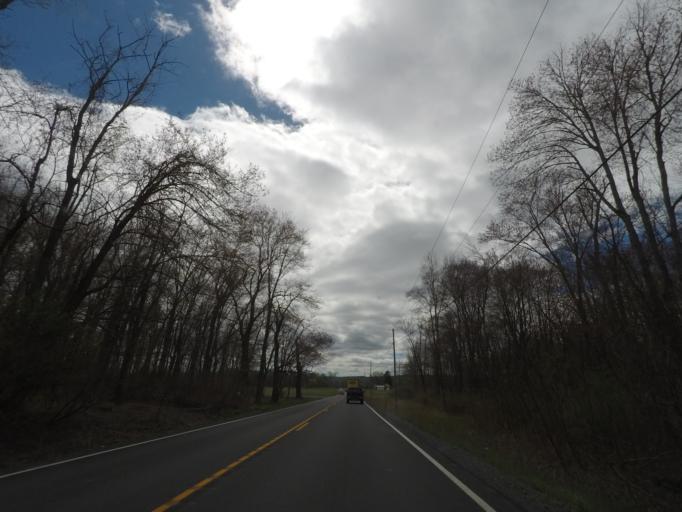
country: US
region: New York
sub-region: Rensselaer County
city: Castleton-on-Hudson
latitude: 42.5053
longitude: -73.7891
